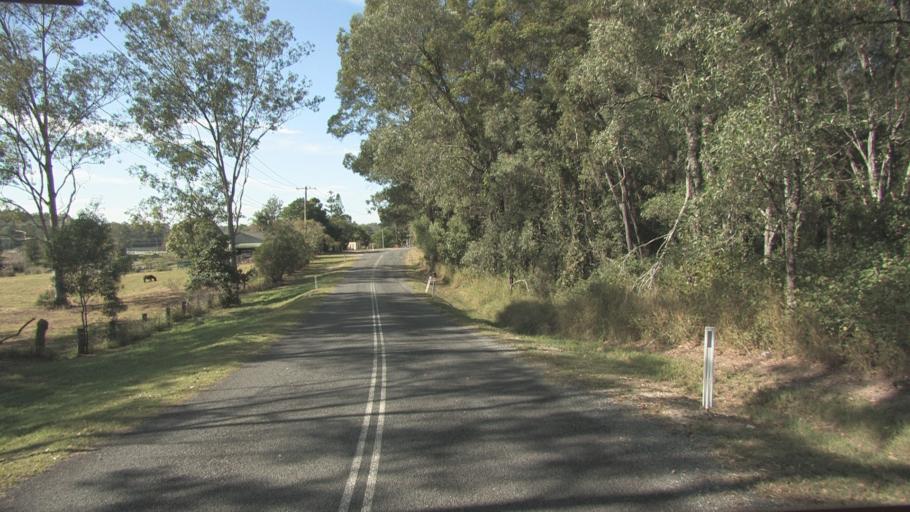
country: AU
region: Queensland
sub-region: Logan
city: Windaroo
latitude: -27.7779
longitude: 153.1822
